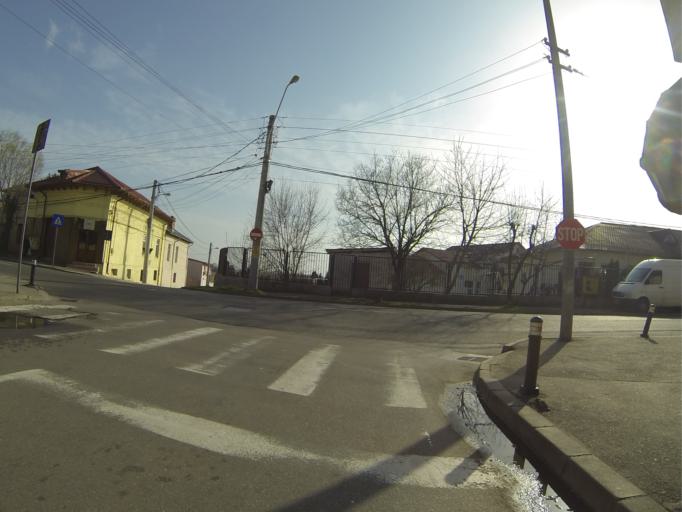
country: RO
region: Dolj
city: Craiova
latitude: 44.3096
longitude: 23.8104
